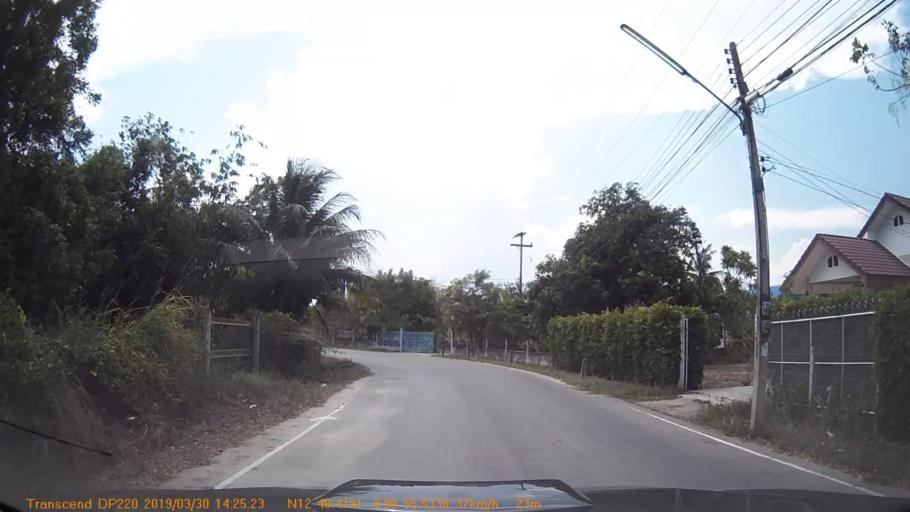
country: TH
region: Prachuap Khiri Khan
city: Hua Hin
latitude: 12.6746
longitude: 99.9256
